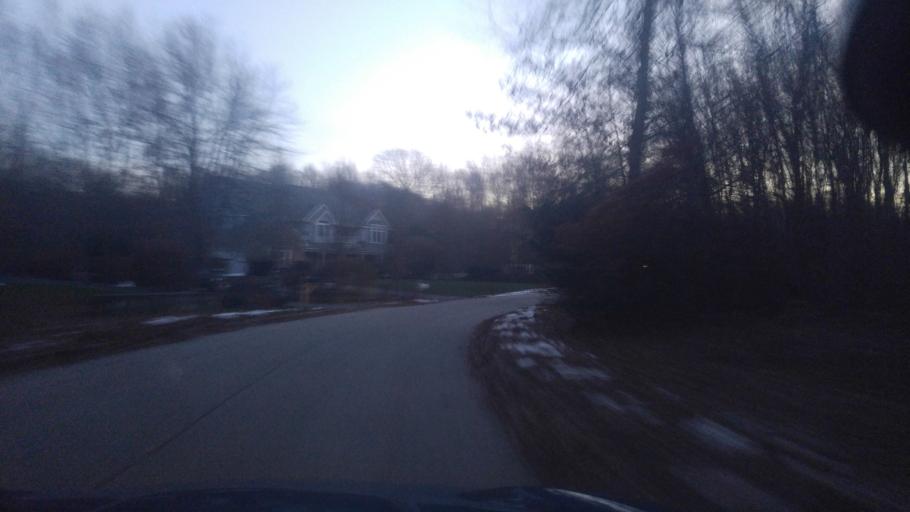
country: US
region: Rhode Island
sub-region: Kent County
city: West Warwick
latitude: 41.6475
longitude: -71.5372
